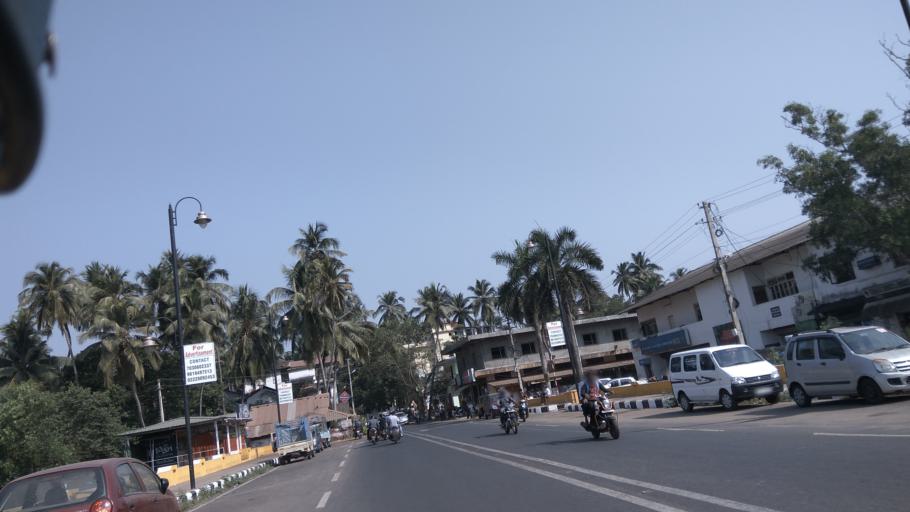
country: IN
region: Goa
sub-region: North Goa
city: Saligao
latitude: 15.5467
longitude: 73.7891
